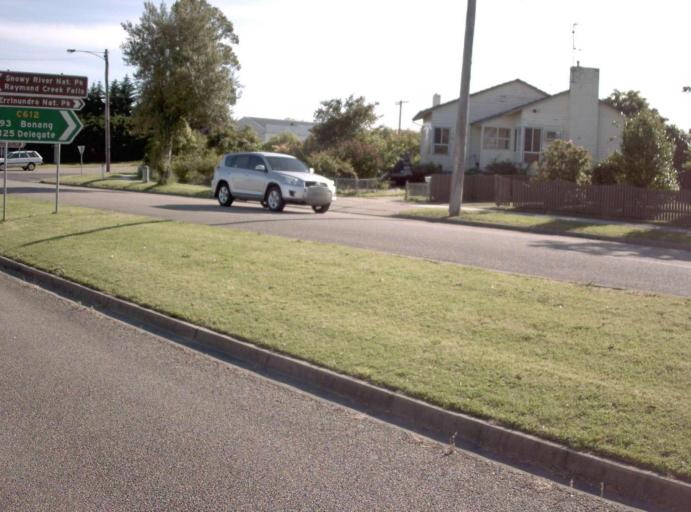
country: AU
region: Victoria
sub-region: East Gippsland
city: Lakes Entrance
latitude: -37.6982
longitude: 148.4570
